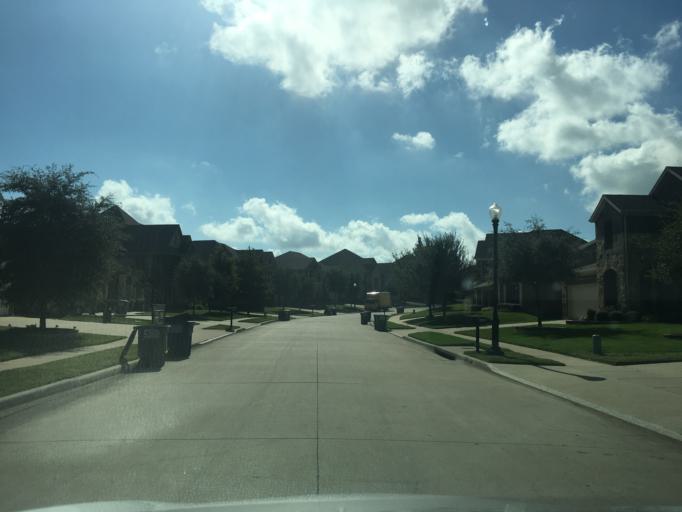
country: US
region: Texas
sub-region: Dallas County
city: Sachse
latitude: 32.9591
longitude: -96.5743
